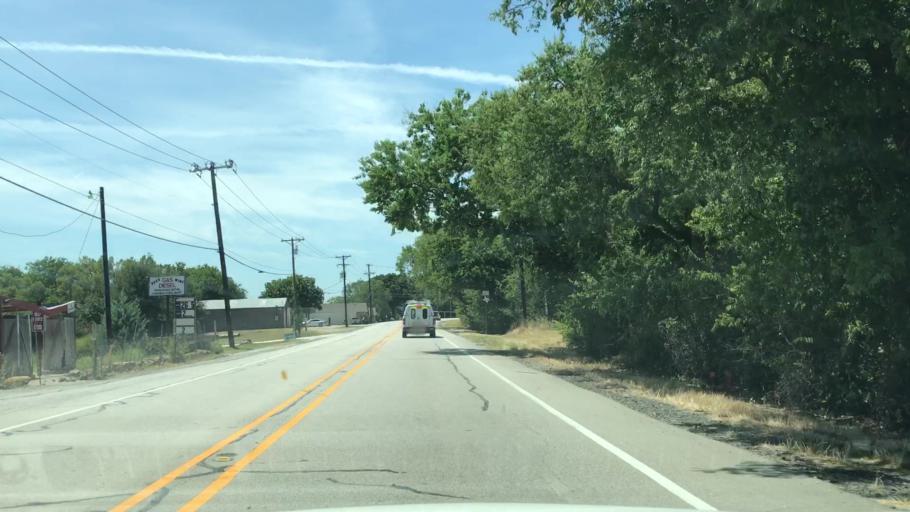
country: US
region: Texas
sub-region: Collin County
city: Fairview
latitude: 33.1596
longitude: -96.6312
